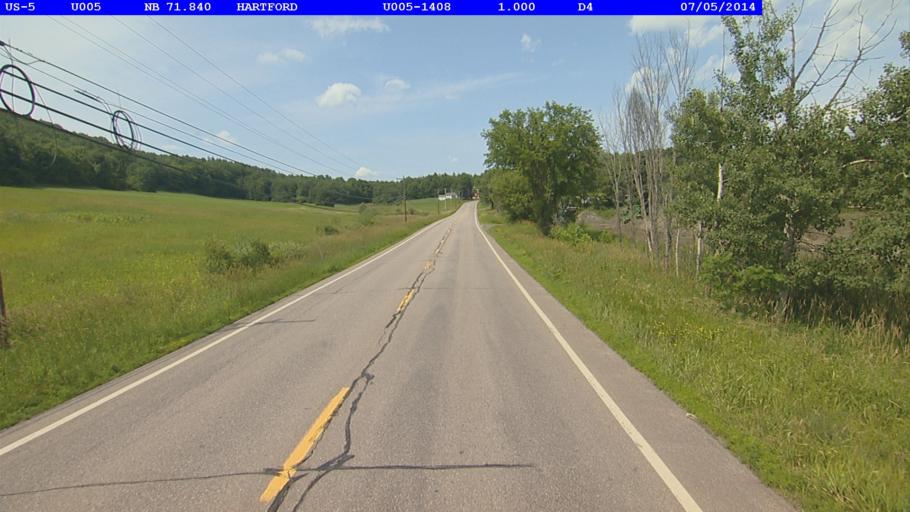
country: US
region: Vermont
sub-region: Windsor County
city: White River Junction
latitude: 43.6249
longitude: -72.3528
